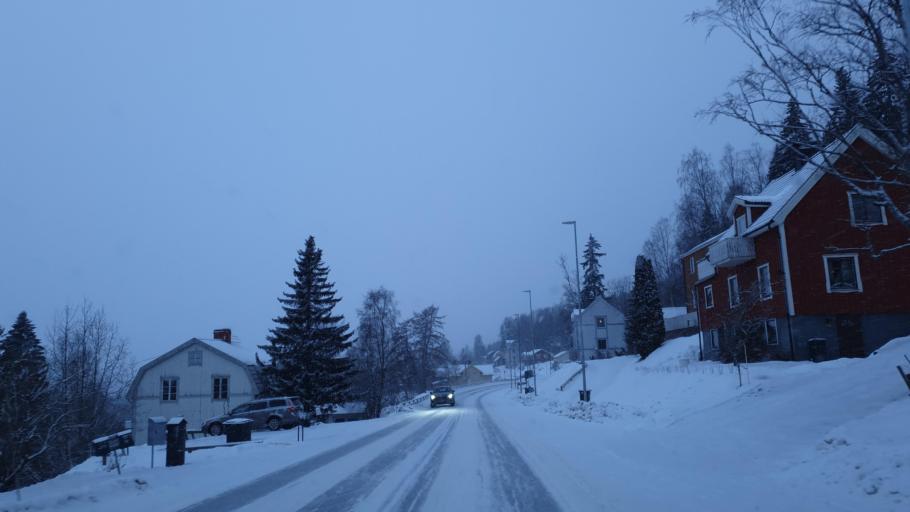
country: SE
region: Vaesternorrland
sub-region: OErnskoeldsviks Kommun
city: Ornskoldsvik
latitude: 63.2982
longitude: 18.6631
